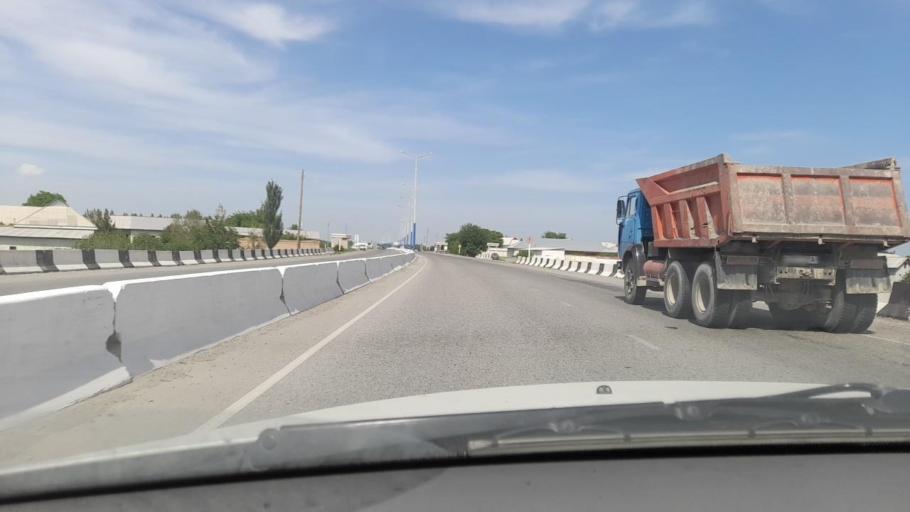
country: UZ
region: Samarqand
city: Kattaqo'rg'on
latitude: 39.9230
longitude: 66.3548
